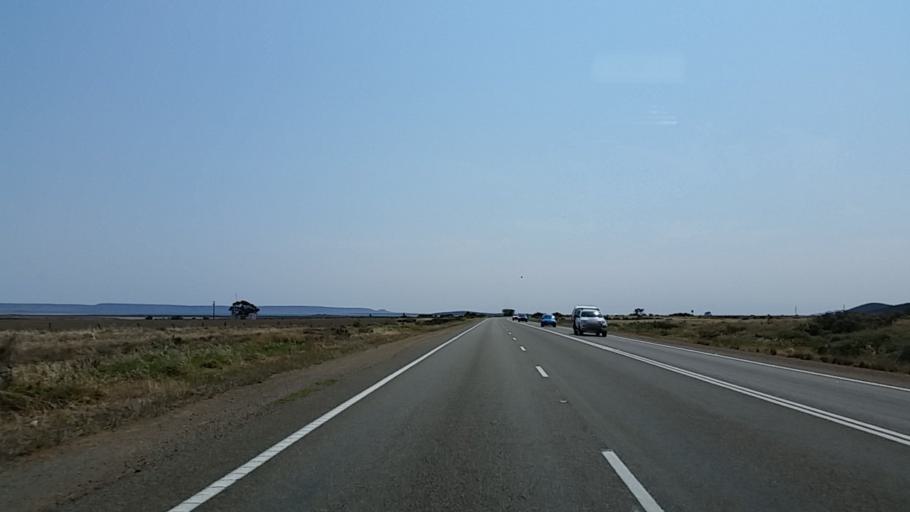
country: AU
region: South Australia
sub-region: Port Augusta
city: Port Augusta
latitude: -32.8081
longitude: 137.9656
